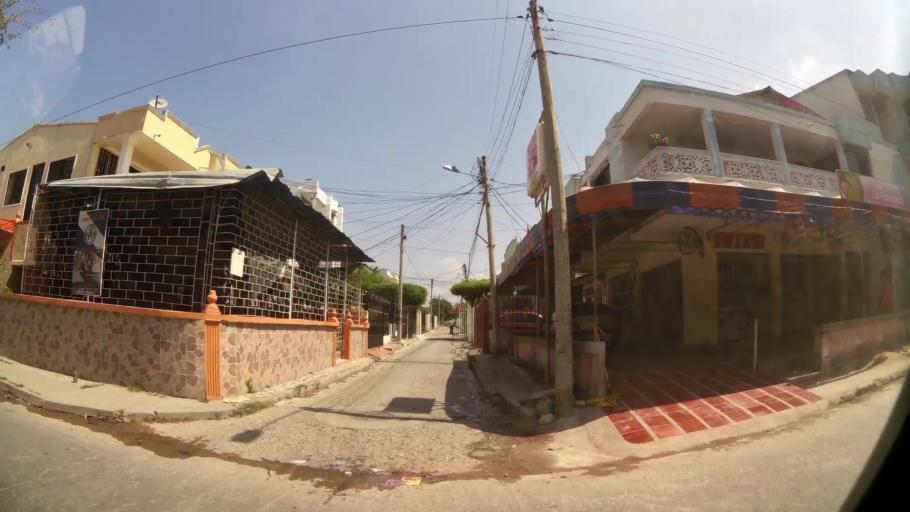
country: CO
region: Bolivar
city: Cartagena
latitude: 10.4004
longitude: -75.4919
